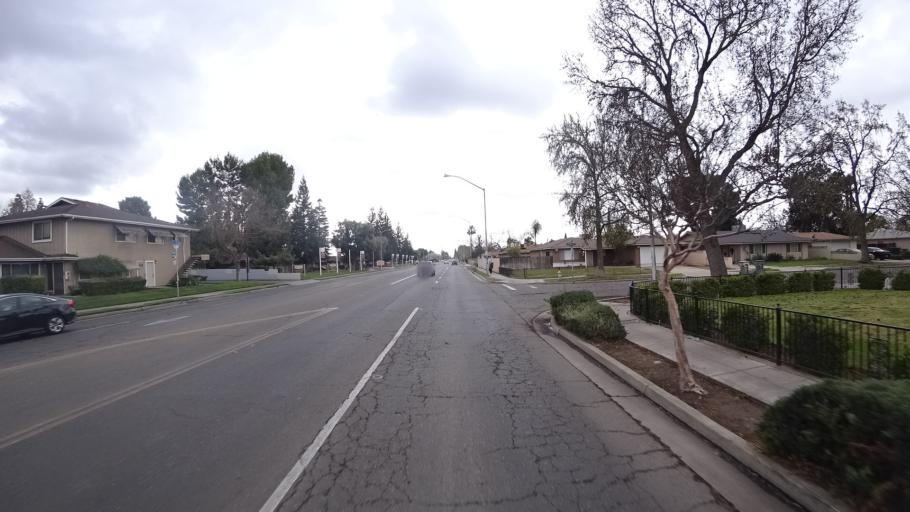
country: US
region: California
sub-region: Fresno County
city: Fresno
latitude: 36.8065
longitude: -119.8445
